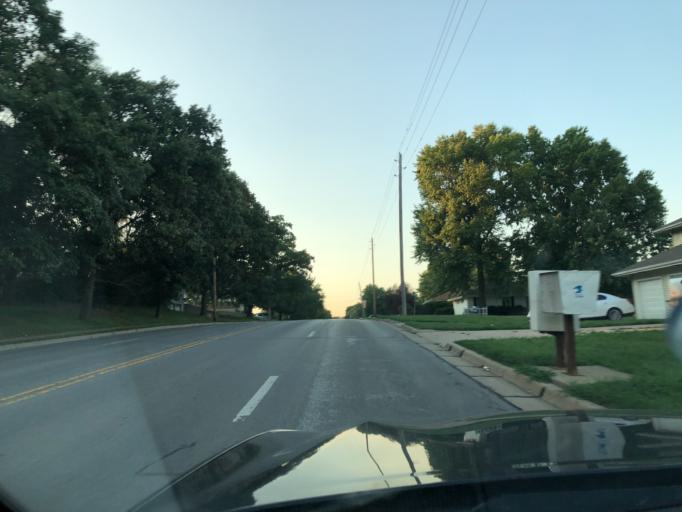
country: US
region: Kansas
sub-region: Leavenworth County
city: Leavenworth
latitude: 39.3124
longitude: -94.9507
